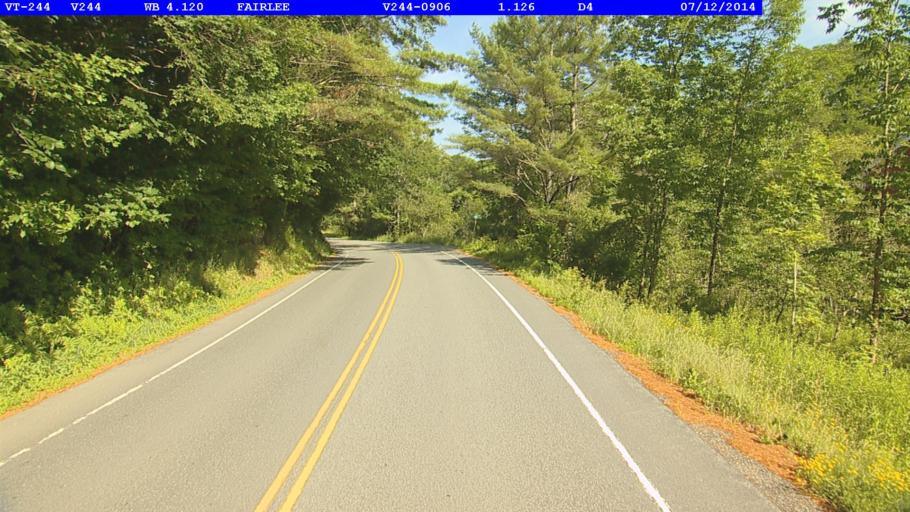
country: US
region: New Hampshire
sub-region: Grafton County
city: Orford
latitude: 43.8922
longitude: -72.1995
